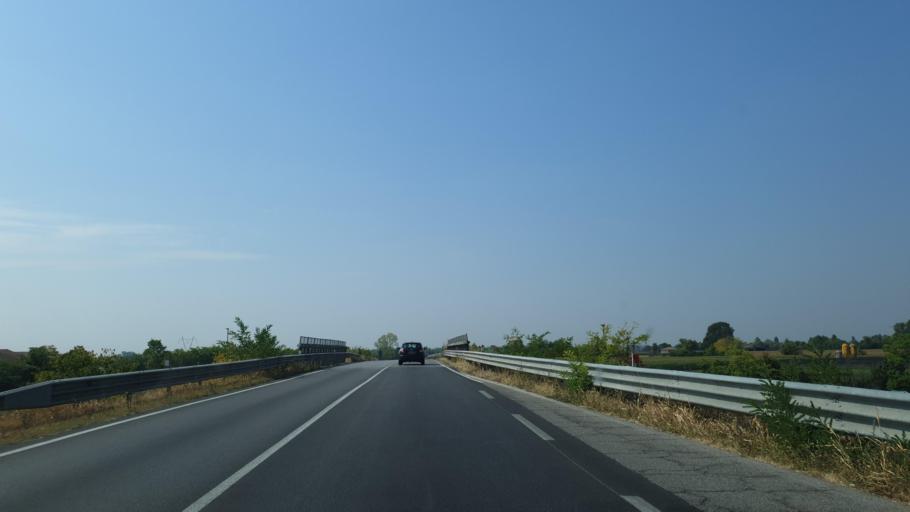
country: IT
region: Lombardy
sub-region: Provincia di Brescia
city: Leno
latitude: 45.3782
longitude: 10.2136
